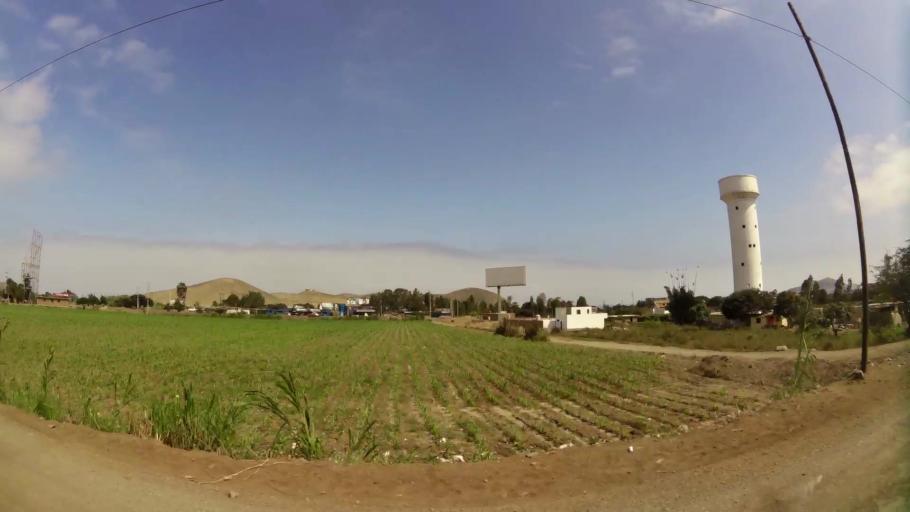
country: PE
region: Lima
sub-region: Provincia de Canete
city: Mala
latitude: -12.7205
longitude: -76.6180
